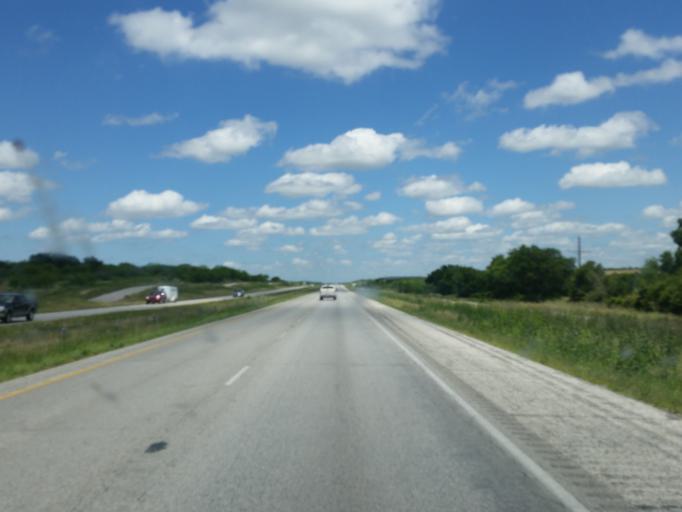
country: US
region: Texas
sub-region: Callahan County
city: Baird
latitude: 32.3837
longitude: -99.2849
